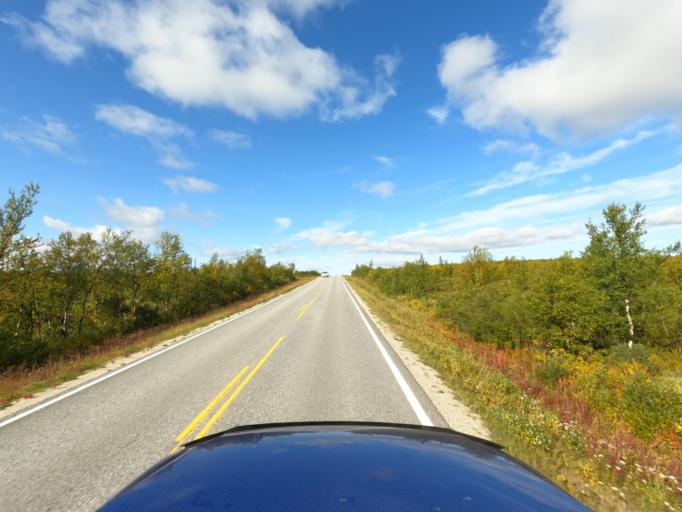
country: NO
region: Finnmark Fylke
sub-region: Karasjok
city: Karasjohka
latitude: 69.5525
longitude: 25.4083
